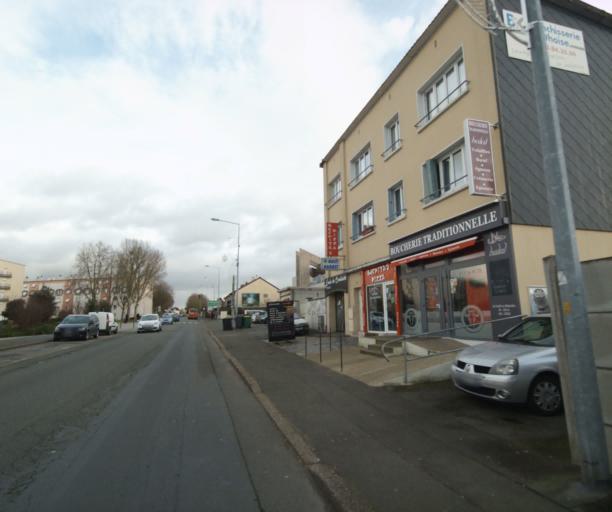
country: FR
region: Pays de la Loire
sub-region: Departement de la Sarthe
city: Le Mans
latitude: 47.9715
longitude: 0.2121
